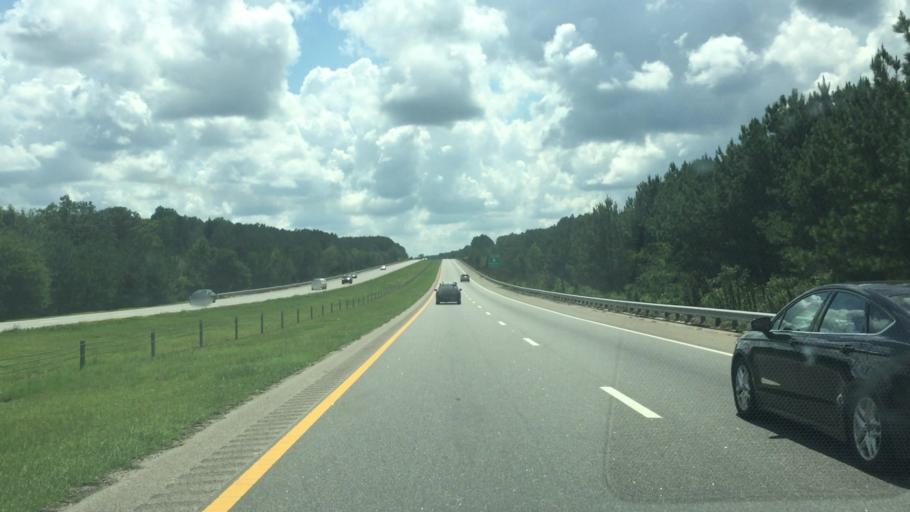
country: US
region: North Carolina
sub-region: Richmond County
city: East Rockingham
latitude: 34.8795
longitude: -79.7772
